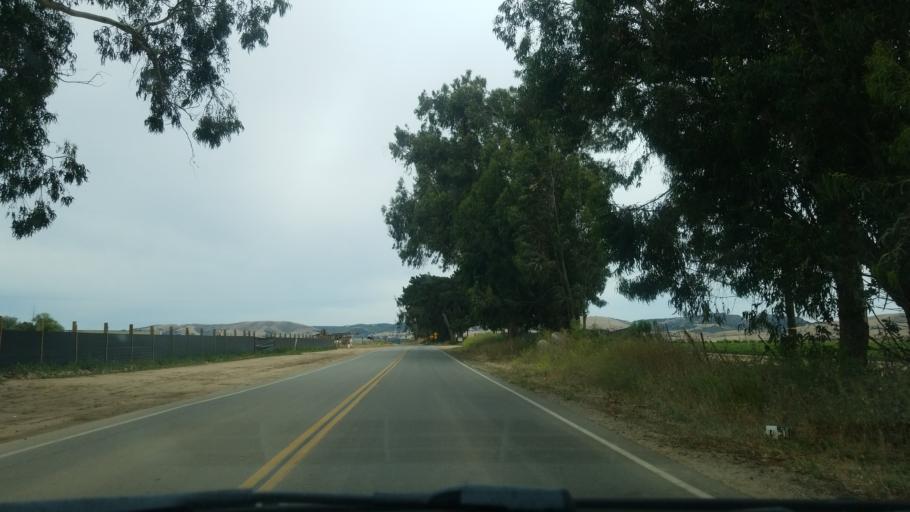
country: US
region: California
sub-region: Santa Barbara County
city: Santa Maria
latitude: 34.9126
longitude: -120.4903
